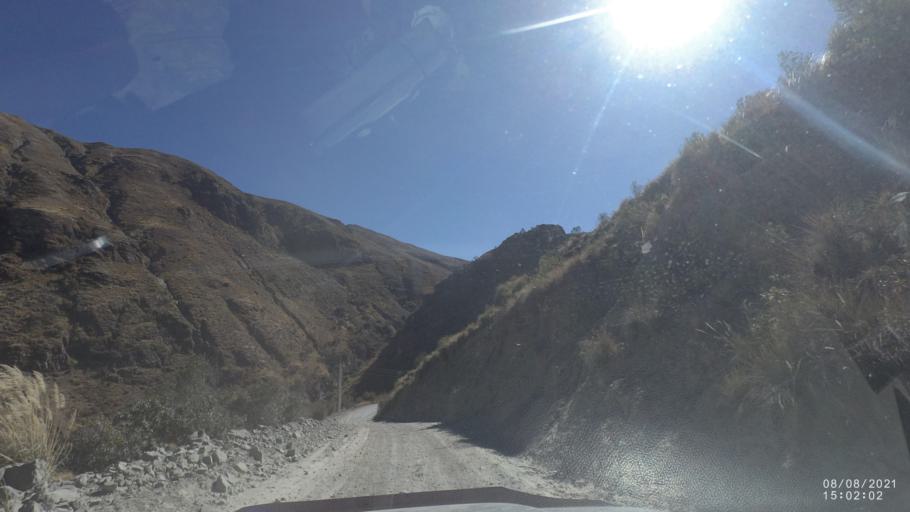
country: BO
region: Cochabamba
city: Sipe Sipe
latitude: -17.2675
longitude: -66.3408
